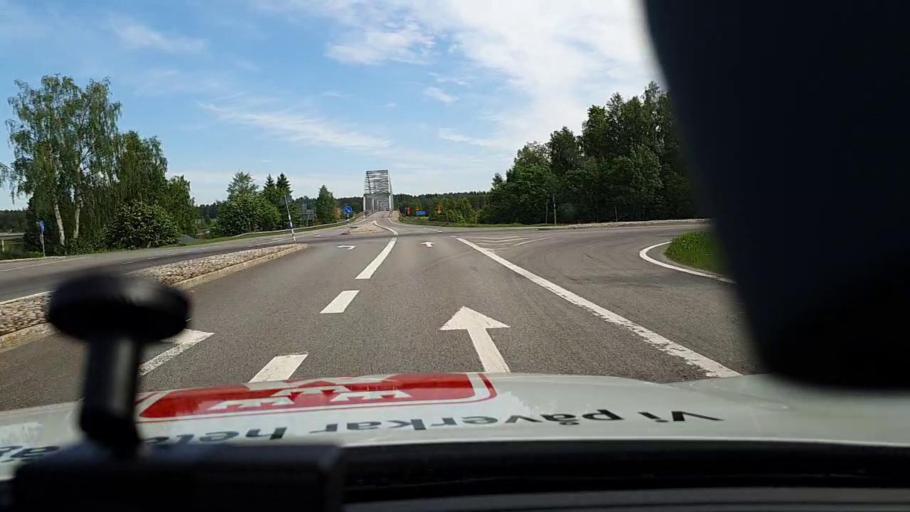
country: SE
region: Norrbotten
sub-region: Lulea Kommun
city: Gammelstad
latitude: 65.5864
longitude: 22.0274
